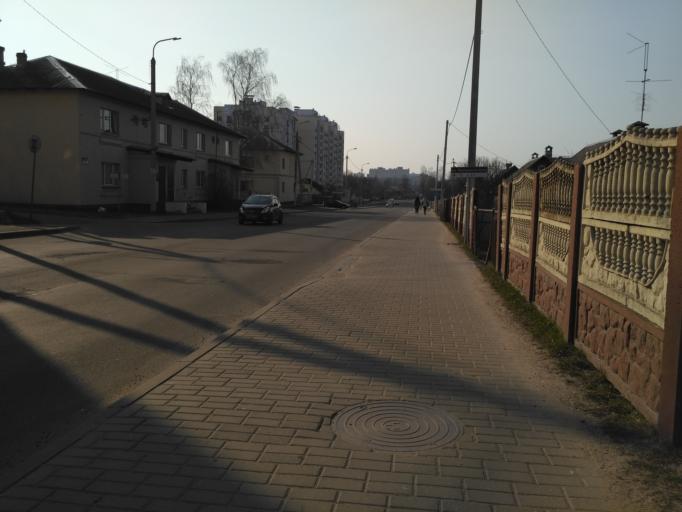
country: BY
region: Minsk
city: Zaslawye
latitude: 54.0077
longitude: 27.2805
